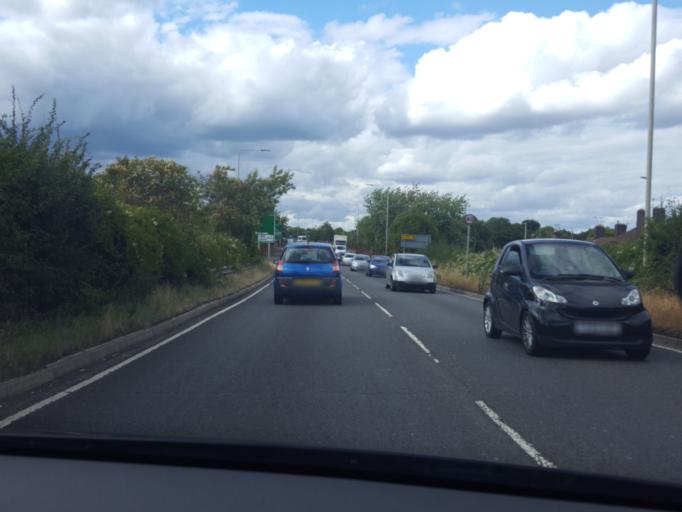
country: GB
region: England
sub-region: Leicestershire
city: Glenfield
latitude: 52.6283
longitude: -1.1875
